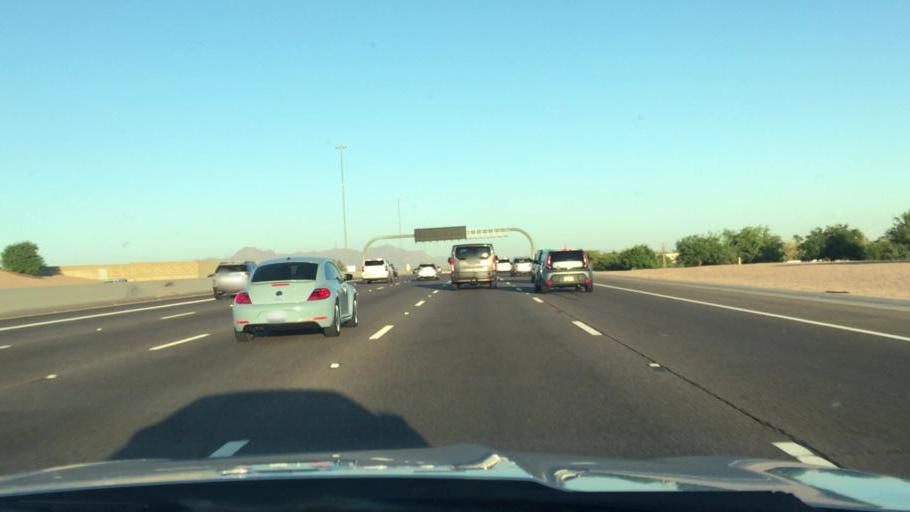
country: US
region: Arizona
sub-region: Maricopa County
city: Gilbert
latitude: 33.3864
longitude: -111.7042
